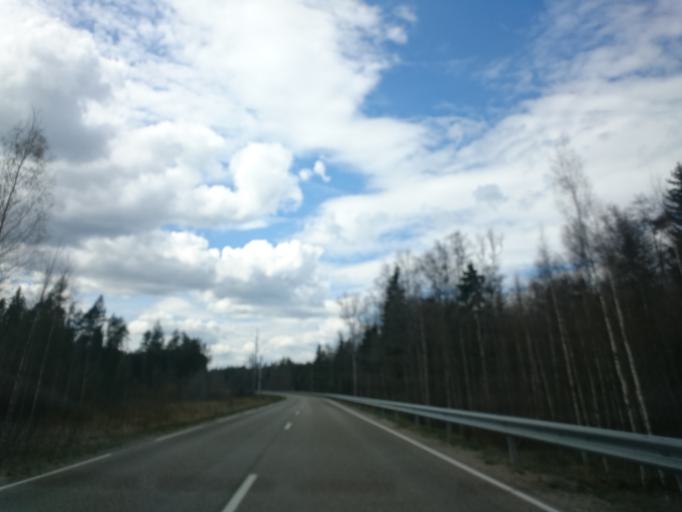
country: LV
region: Talsu Rajons
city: Sabile
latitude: 56.9531
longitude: 22.2988
